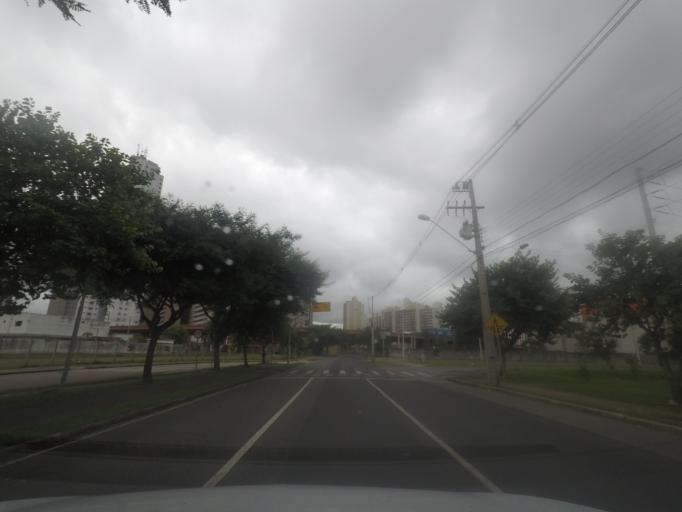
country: BR
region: Parana
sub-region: Curitiba
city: Curitiba
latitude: -25.4371
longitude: -49.2546
